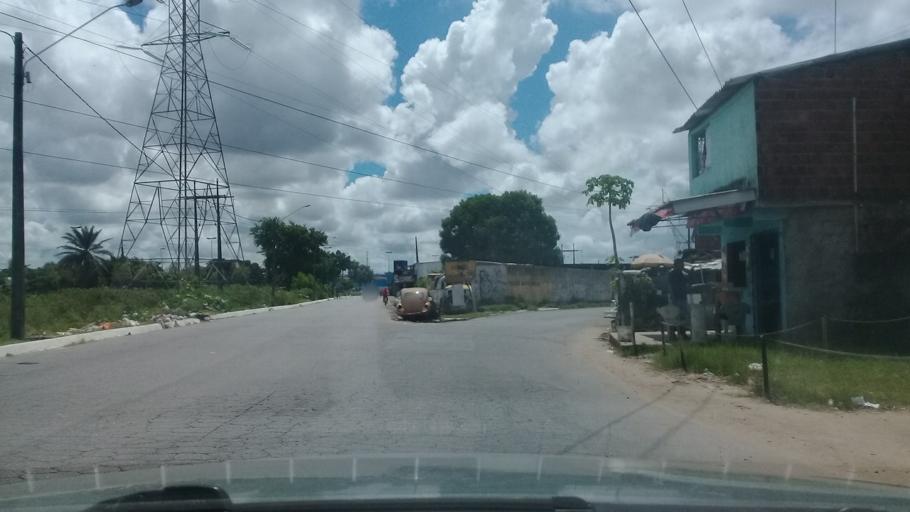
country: BR
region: Pernambuco
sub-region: Recife
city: Recife
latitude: -8.0671
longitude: -34.9397
